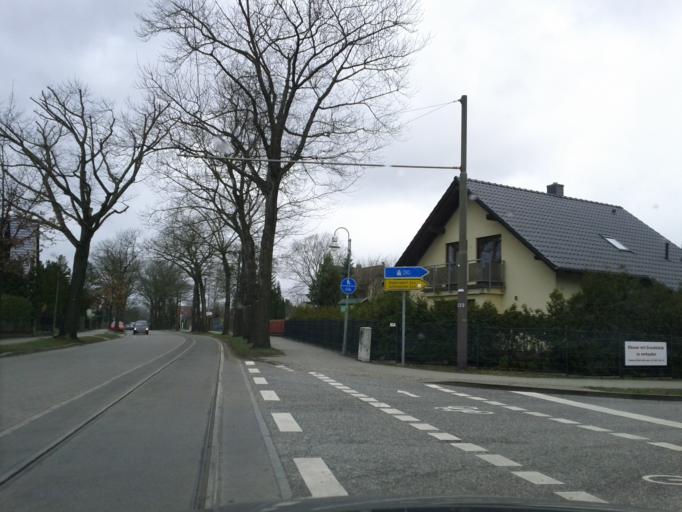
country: DE
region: Brandenburg
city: Woltersdorf
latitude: 52.4522
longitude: 13.7484
